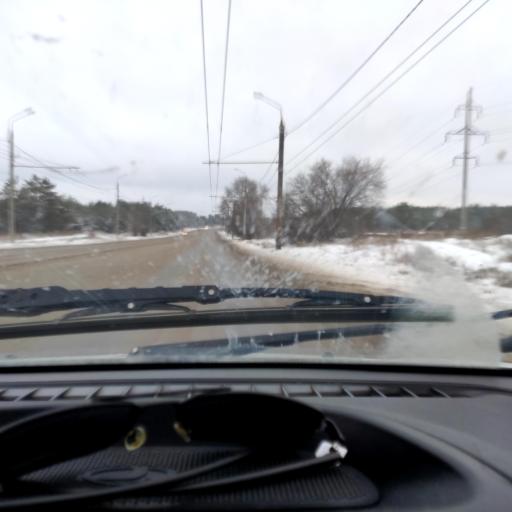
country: RU
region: Samara
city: Zhigulevsk
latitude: 53.5041
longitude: 49.5158
